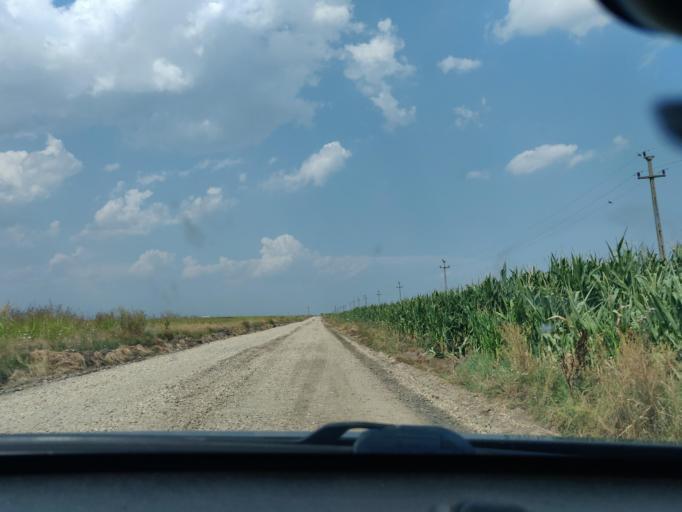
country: RO
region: Teleorman
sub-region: Comuna Sarbeni
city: Sarbeni
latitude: 44.4905
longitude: 25.3928
